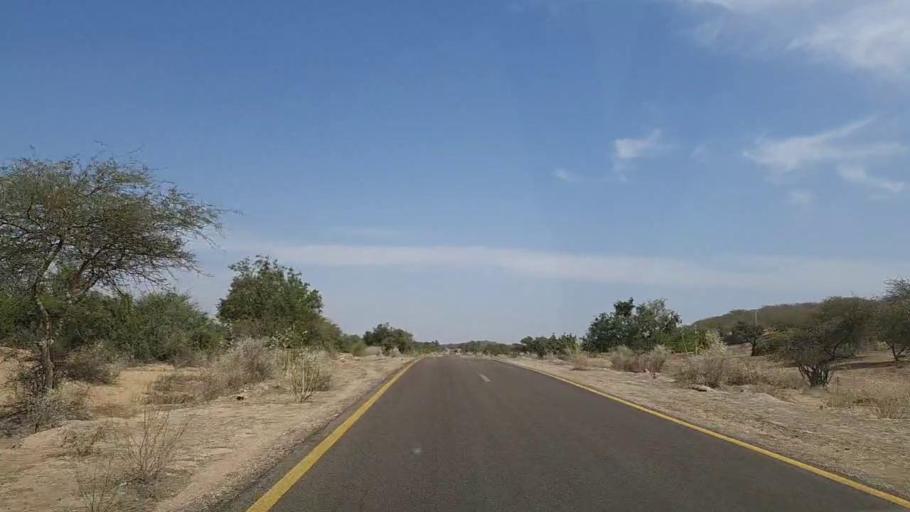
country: PK
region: Sindh
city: Mithi
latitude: 24.8806
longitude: 69.8672
